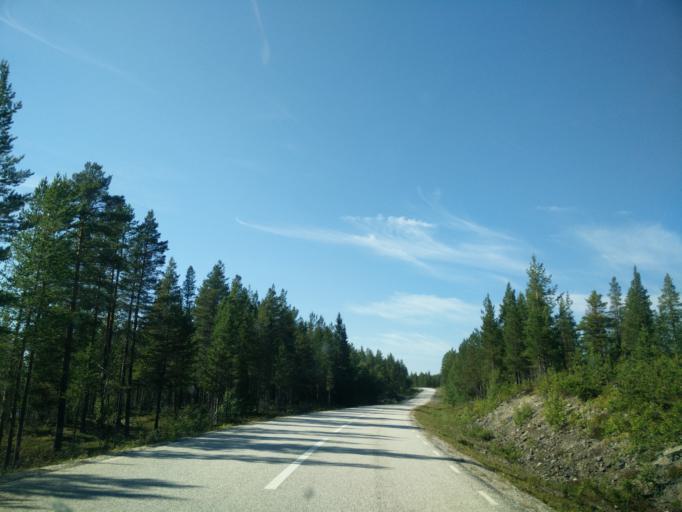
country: SE
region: Jaemtland
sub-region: Are Kommun
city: Jarpen
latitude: 62.8292
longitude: 13.4557
